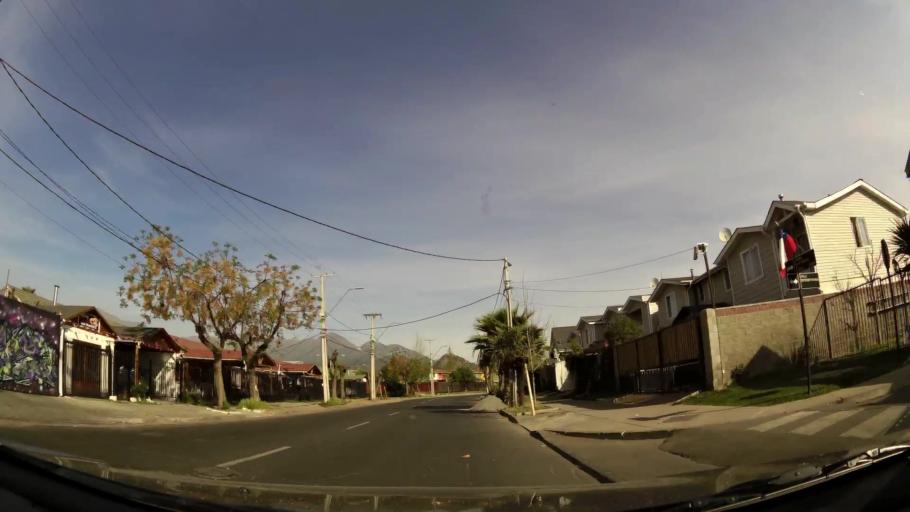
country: CL
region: Santiago Metropolitan
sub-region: Provincia de Cordillera
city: Puente Alto
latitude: -33.5906
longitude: -70.5560
